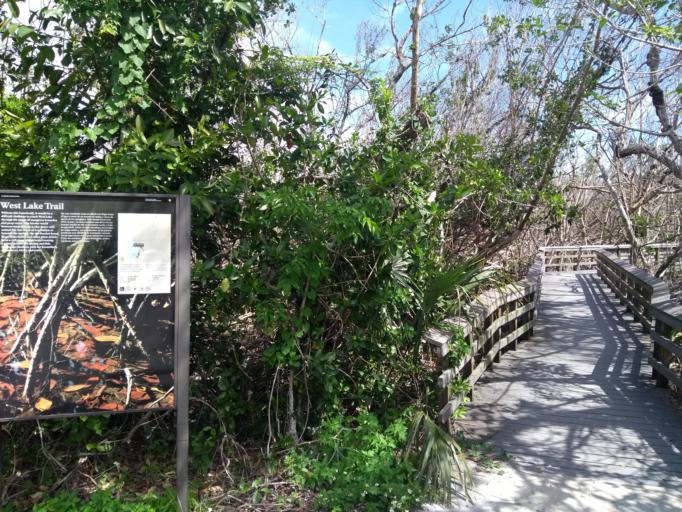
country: US
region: Florida
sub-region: Monroe County
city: Islamorada
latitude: 25.2143
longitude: -80.8508
